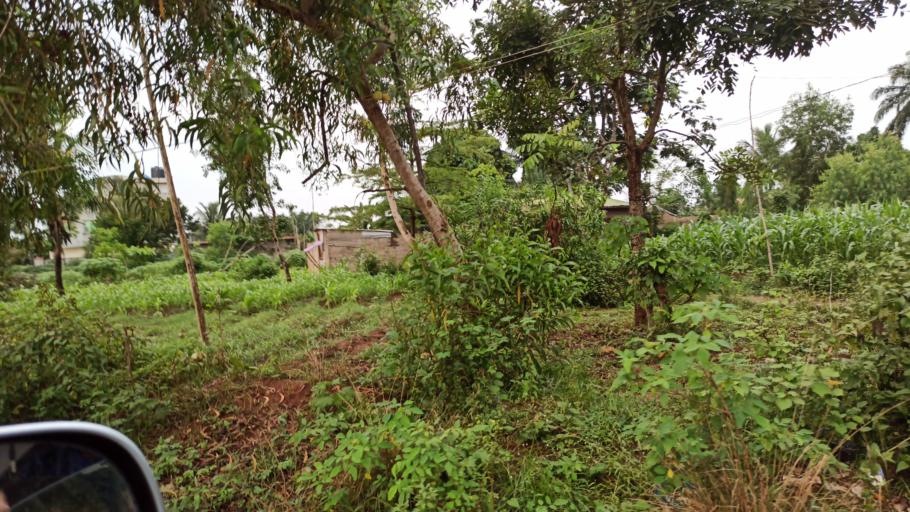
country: BJ
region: Queme
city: Porto-Novo
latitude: 6.4888
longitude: 2.6662
